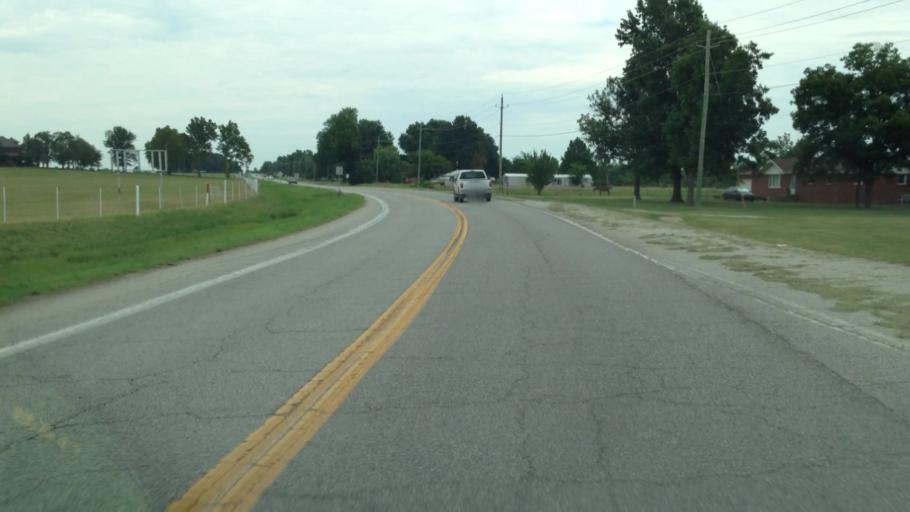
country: US
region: Oklahoma
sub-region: Craig County
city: Vinita
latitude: 36.6573
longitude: -95.1438
